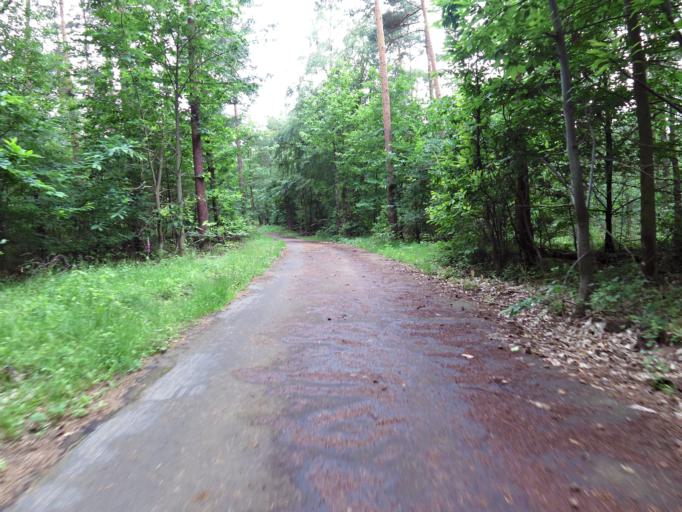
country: DE
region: Rheinland-Pfalz
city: Weisenheim am Berg
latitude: 49.4884
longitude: 8.1223
